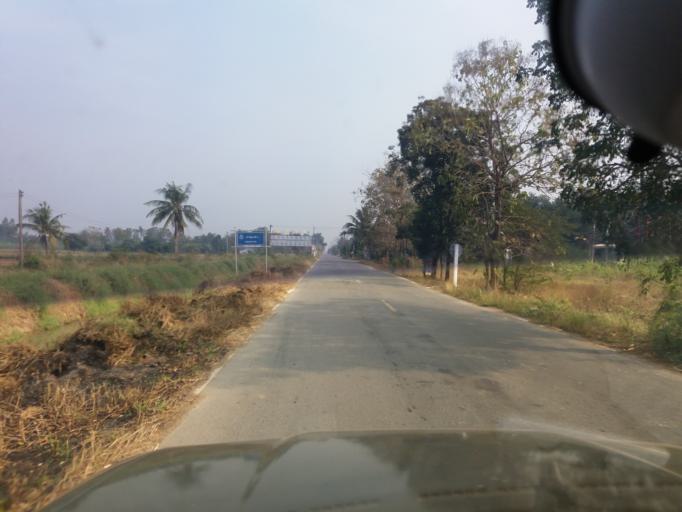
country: TH
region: Suphan Buri
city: Doem Bang Nang Buat
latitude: 14.8736
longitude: 100.1743
